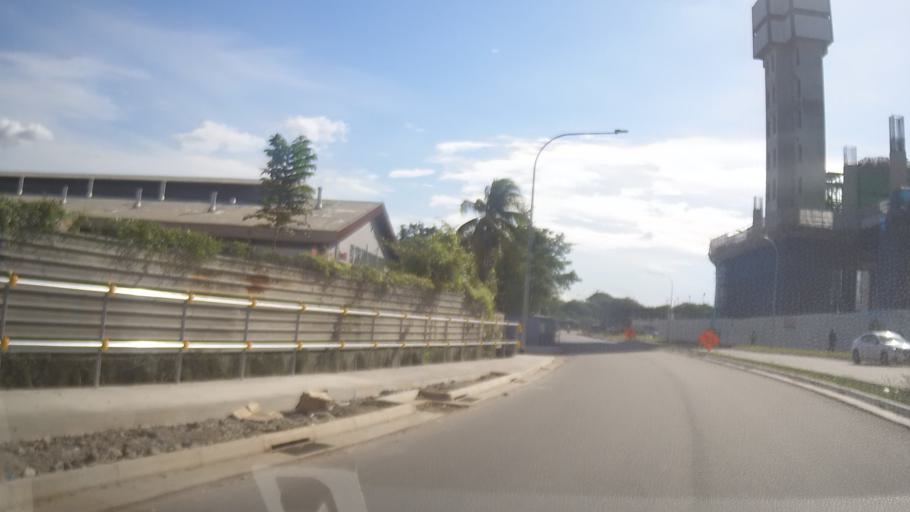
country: MY
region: Johor
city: Johor Bahru
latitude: 1.4370
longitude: 103.7564
